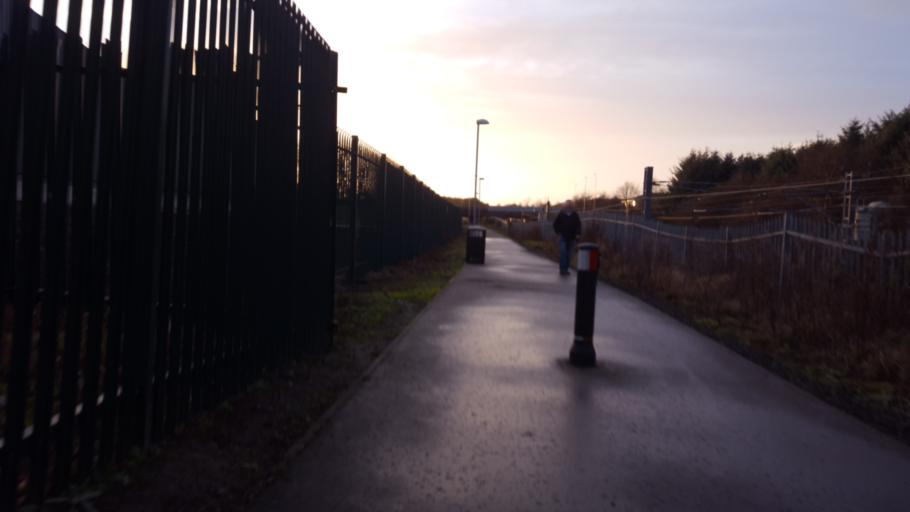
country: GB
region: Scotland
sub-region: West Lothian
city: Livingston
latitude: 55.9147
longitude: -3.5205
